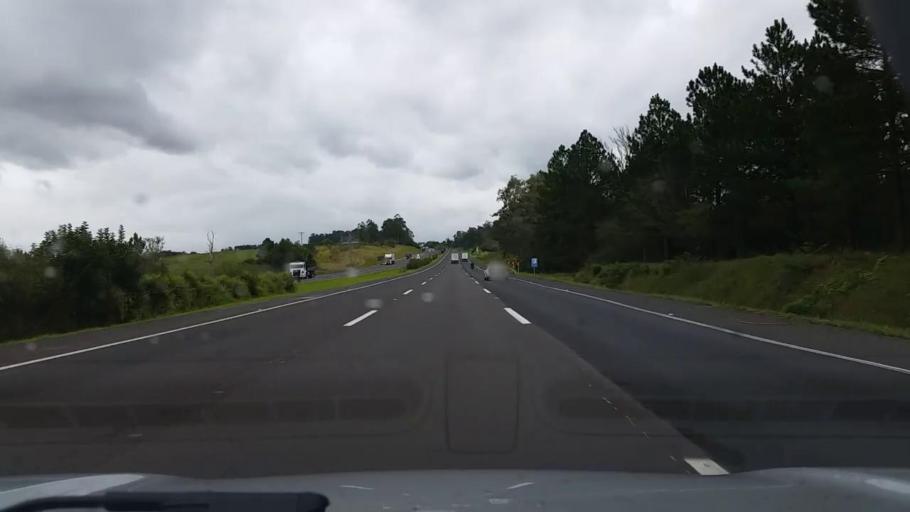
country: BR
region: Rio Grande do Sul
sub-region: Gravatai
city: Gravatai
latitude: -29.9266
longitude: -50.8644
